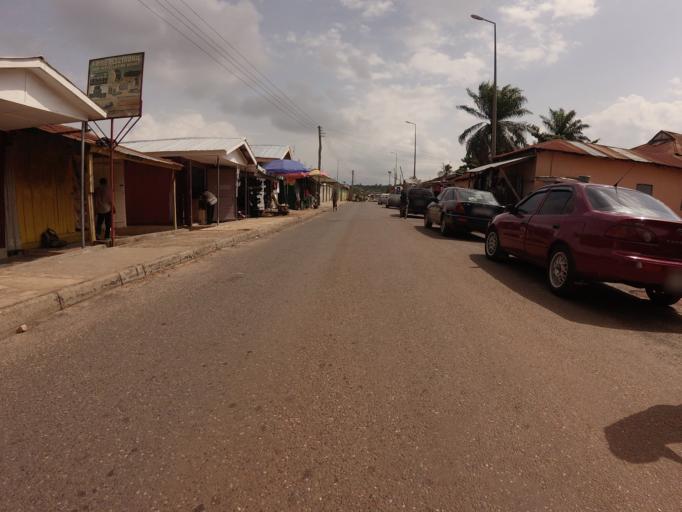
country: GH
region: Volta
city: Ho
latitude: 6.6157
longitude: 0.4711
